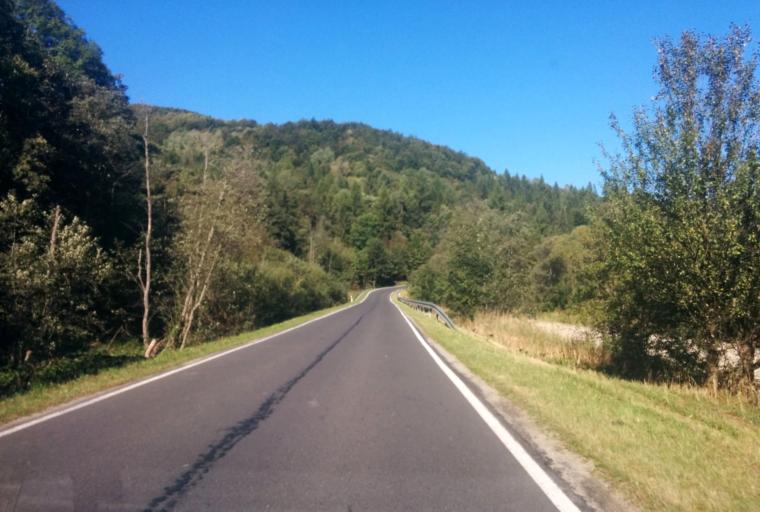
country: PL
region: Subcarpathian Voivodeship
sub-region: Powiat bieszczadzki
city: Lutowiska
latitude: 49.1275
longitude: 22.6690
